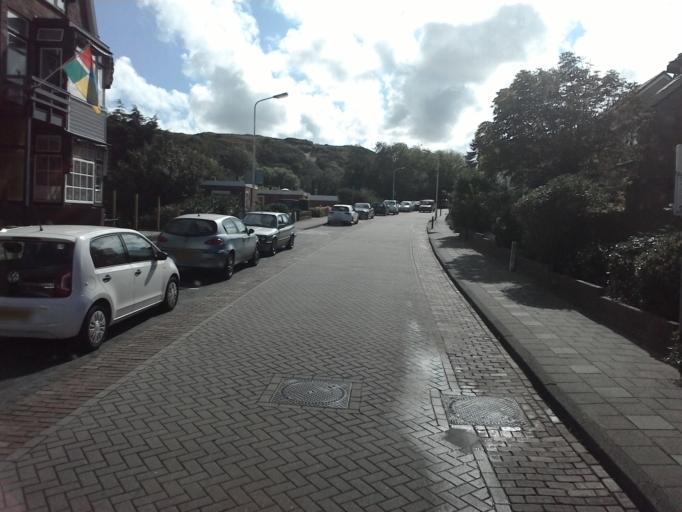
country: NL
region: North Holland
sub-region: Gemeente Beverwijk
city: Beverwijk
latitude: 52.4917
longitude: 4.5925
